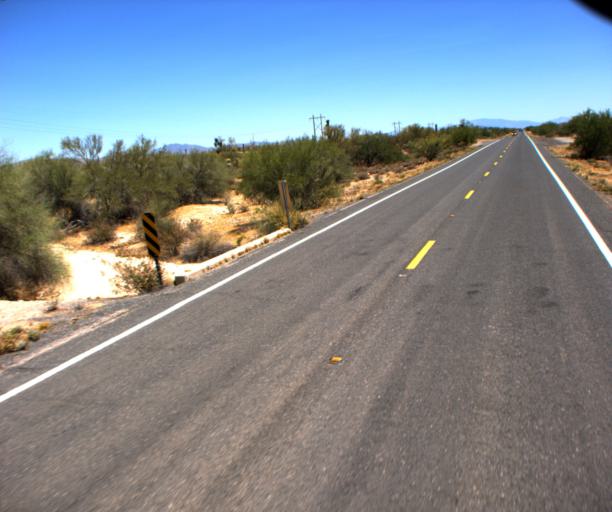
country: US
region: Arizona
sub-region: Pinal County
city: Florence
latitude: 32.8618
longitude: -111.2416
